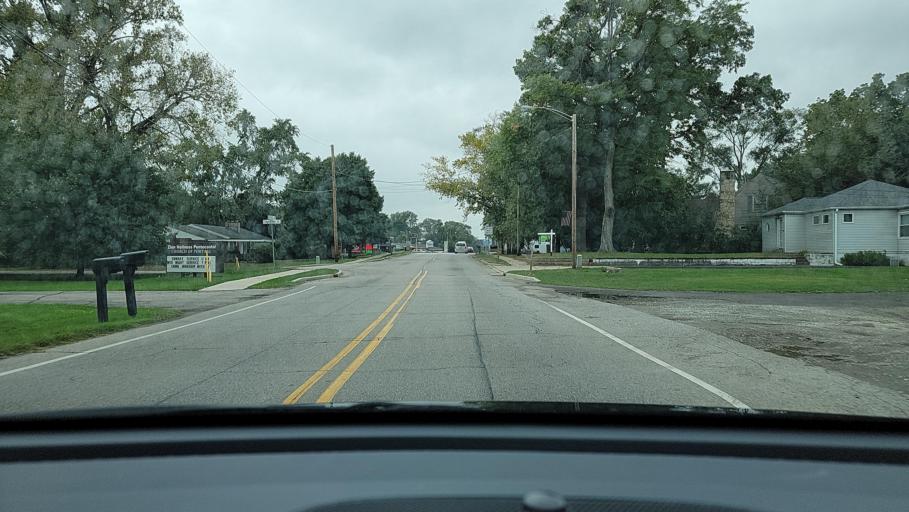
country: US
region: Indiana
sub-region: Lake County
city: Lake Station
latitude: 41.5748
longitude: -87.2199
